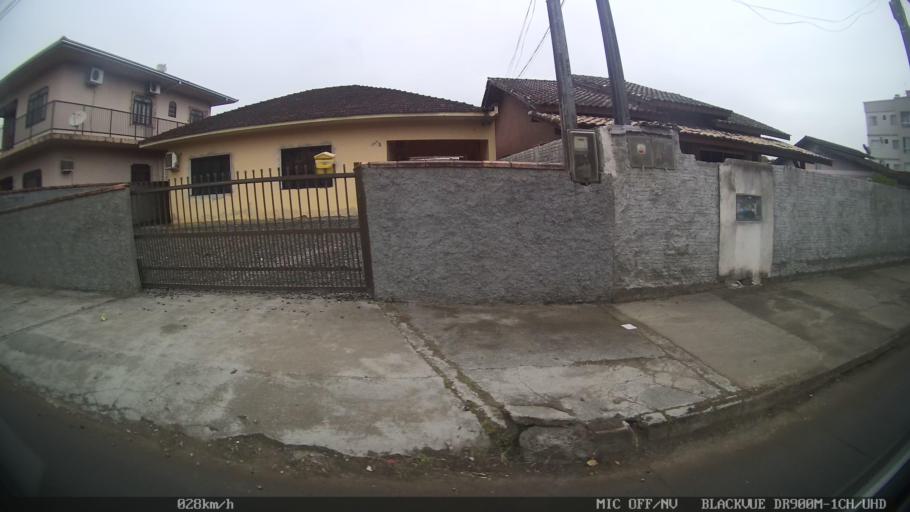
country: BR
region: Santa Catarina
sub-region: Joinville
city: Joinville
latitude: -26.2360
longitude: -48.8088
